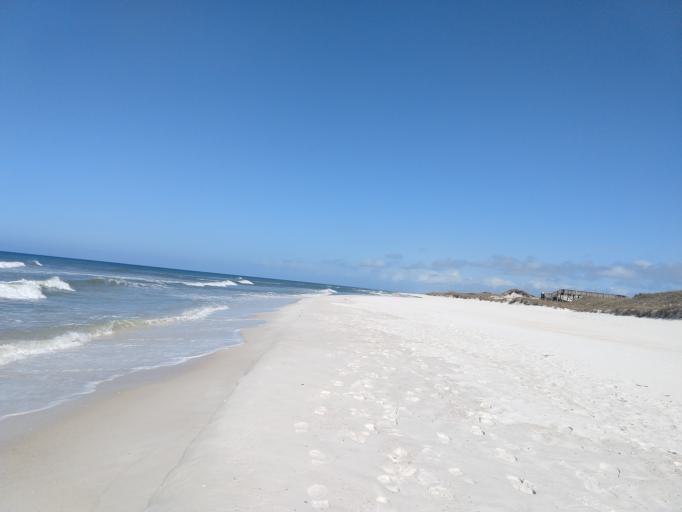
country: US
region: Florida
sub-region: Gulf County
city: Port Saint Joe
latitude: 29.7648
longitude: -85.4050
